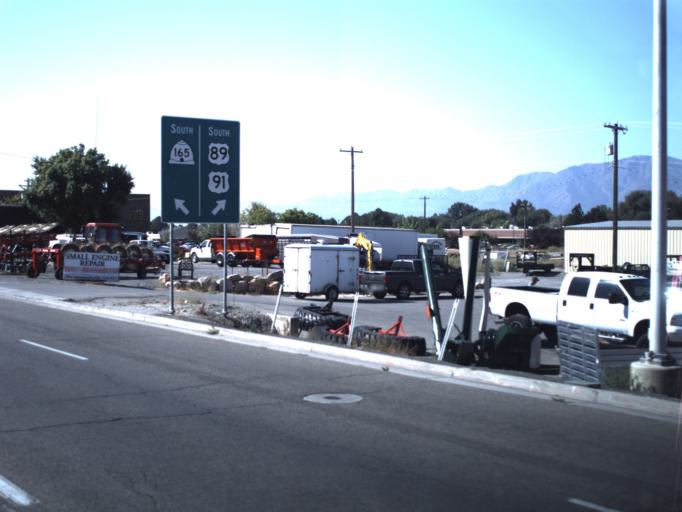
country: US
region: Utah
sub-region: Cache County
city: River Heights
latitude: 41.7193
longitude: -111.8354
